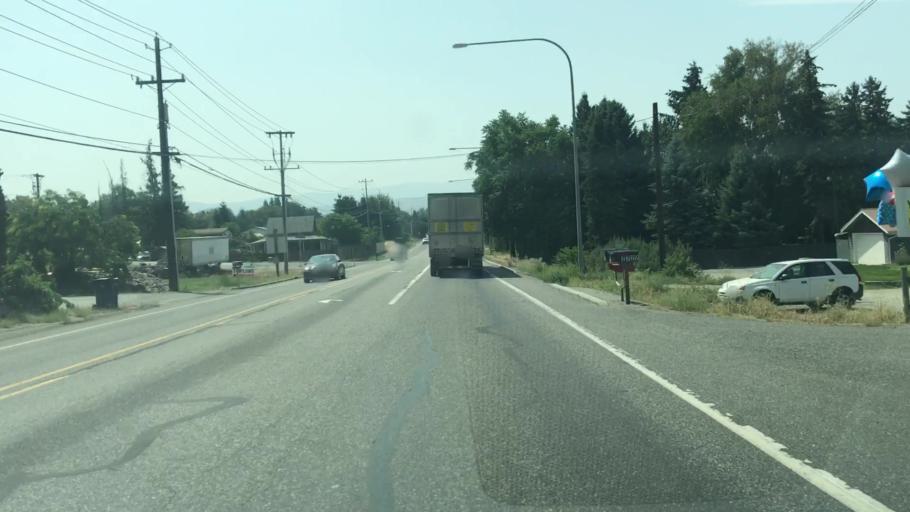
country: US
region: Washington
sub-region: Douglas County
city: East Wenatchee Bench
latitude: 47.4508
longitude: -120.2974
